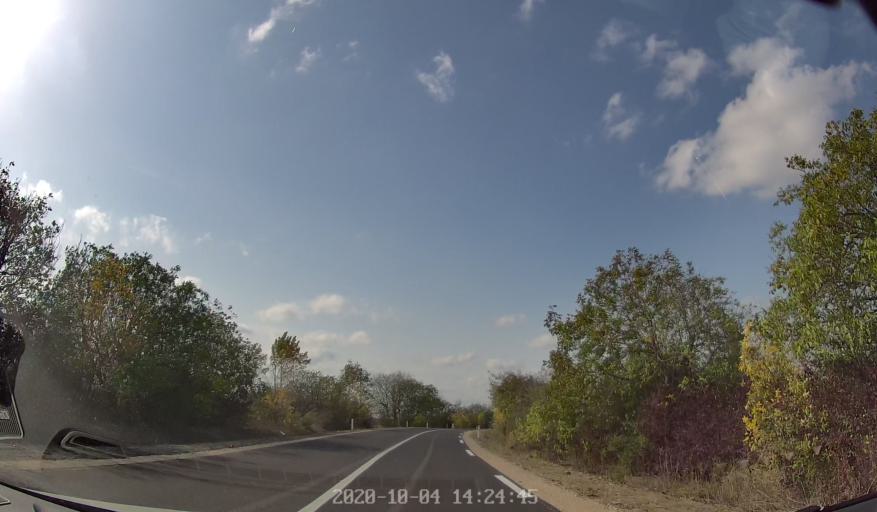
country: MD
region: Rezina
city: Saharna
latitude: 47.6156
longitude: 28.9107
